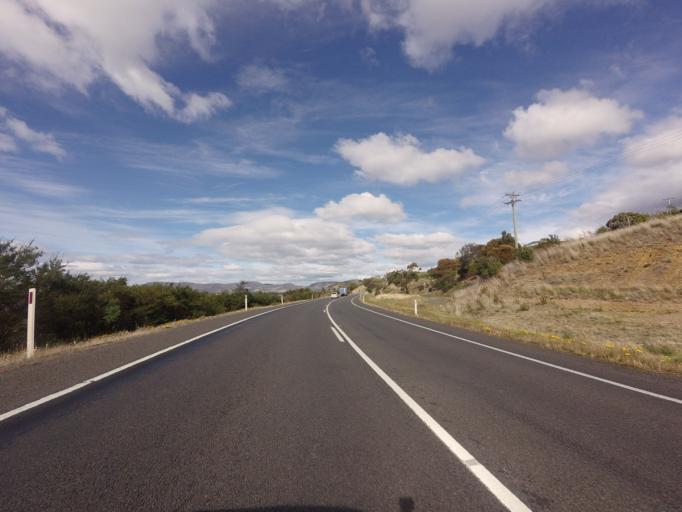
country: AU
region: Tasmania
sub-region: Brighton
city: Bridgewater
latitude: -42.7412
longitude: 147.2074
